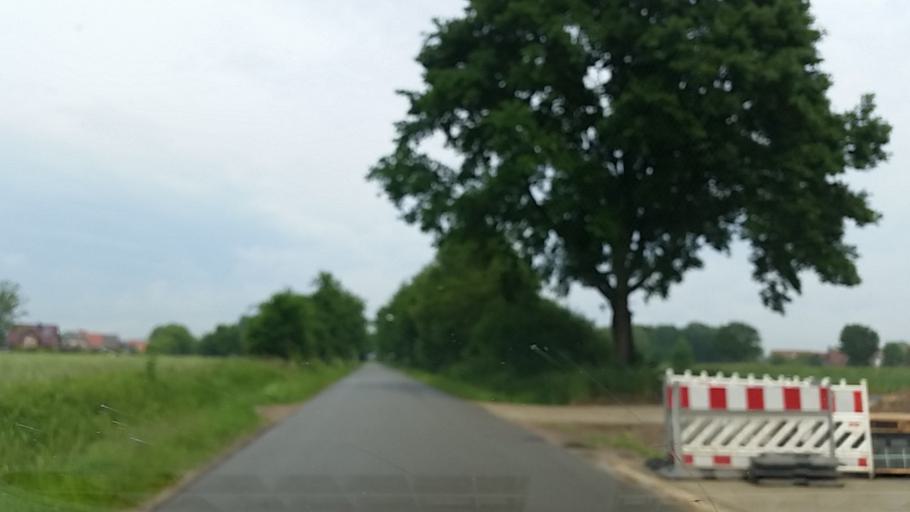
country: DE
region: Schleswig-Holstein
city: Escheburg
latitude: 53.4212
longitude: 10.3167
